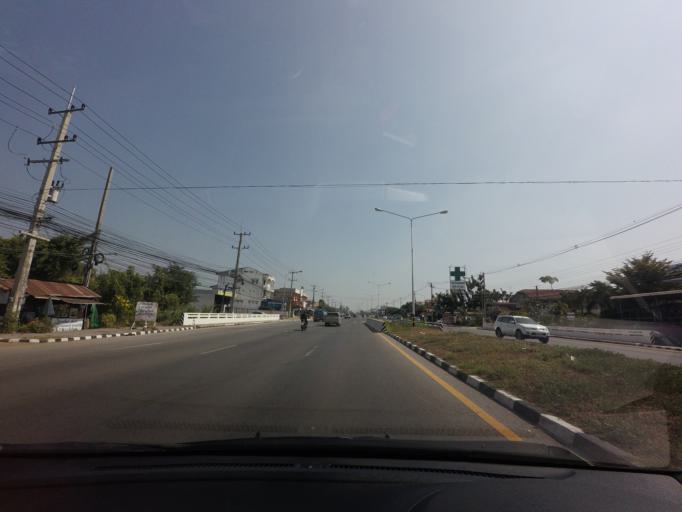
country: TH
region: Sukhothai
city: Sukhothai
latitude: 17.0098
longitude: 99.7992
